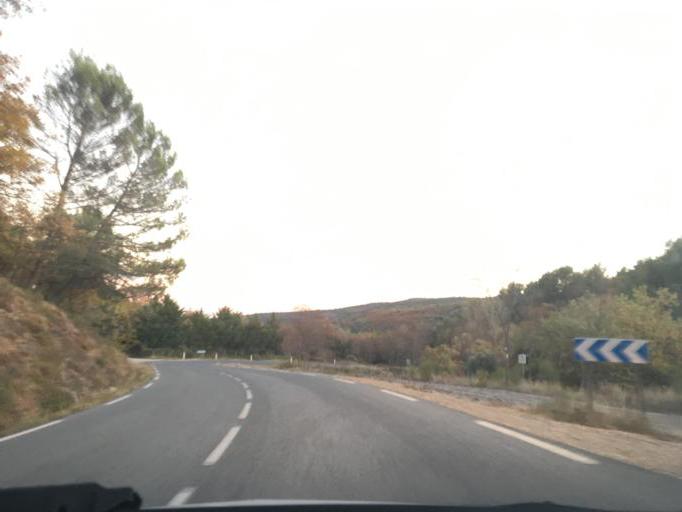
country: FR
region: Provence-Alpes-Cote d'Azur
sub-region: Departement du Var
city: Montferrat
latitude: 43.6334
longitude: 6.4864
